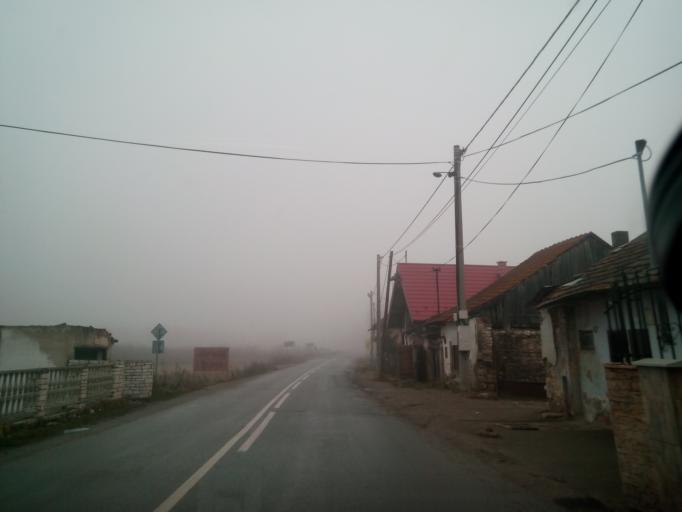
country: SK
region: Presovsky
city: Spisske Podhradie
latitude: 48.9696
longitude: 20.7836
